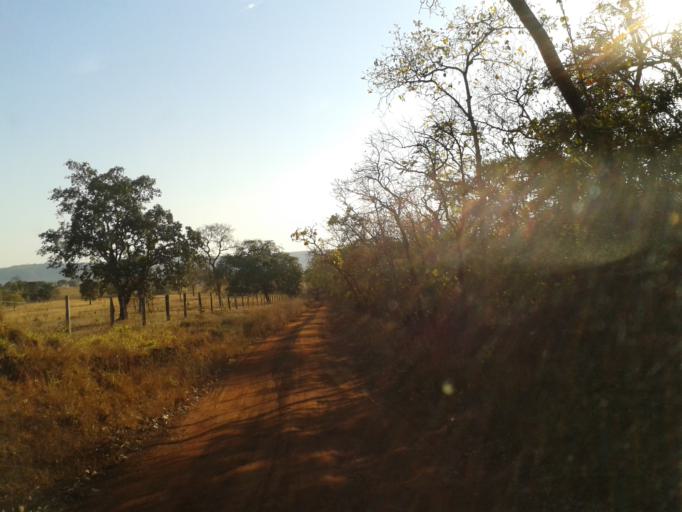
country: BR
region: Minas Gerais
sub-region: Santa Vitoria
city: Santa Vitoria
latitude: -19.1842
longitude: -50.0287
